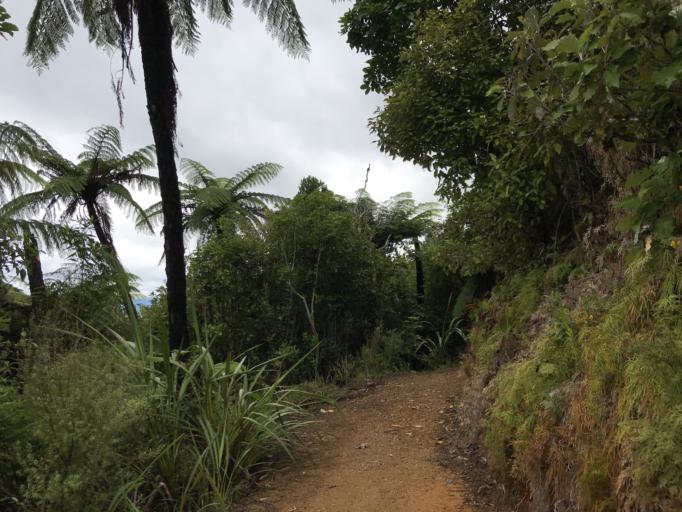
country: NZ
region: Marlborough
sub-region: Marlborough District
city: Picton
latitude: -41.1068
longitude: 174.1446
